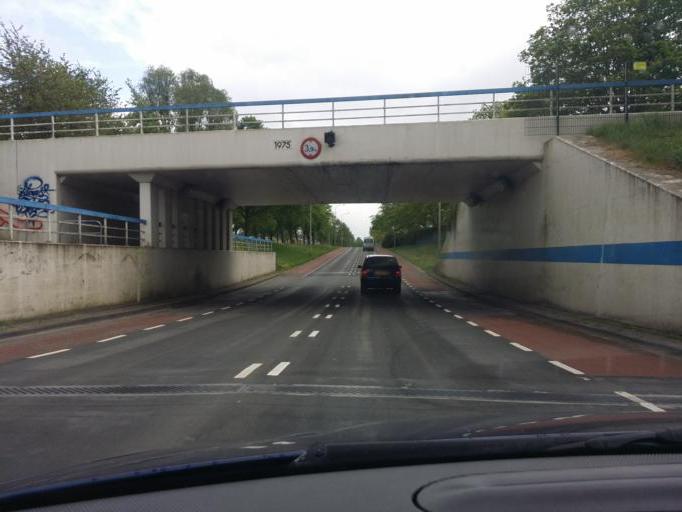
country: NL
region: Groningen
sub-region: Gemeente Hoogezand-Sappemeer
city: Hoogezand
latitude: 53.1610
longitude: 6.7395
